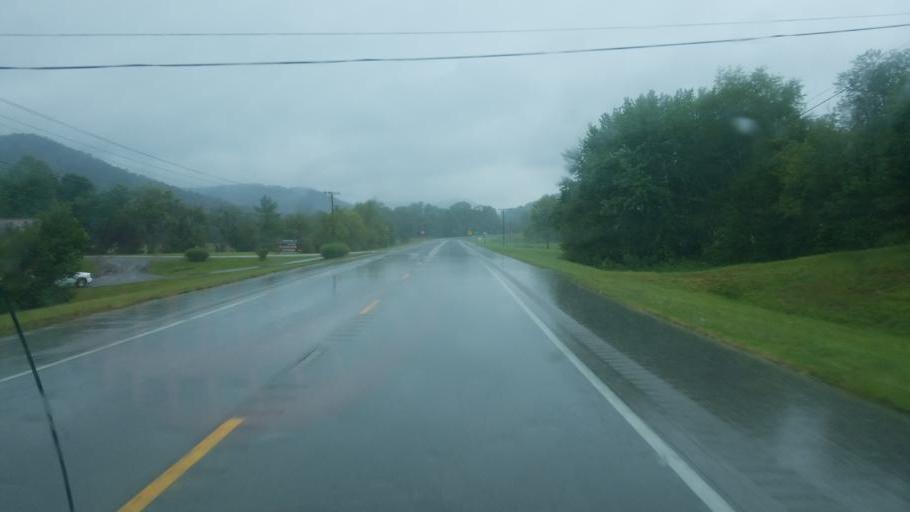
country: US
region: Kentucky
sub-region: Lewis County
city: Vanceburg
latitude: 38.5767
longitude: -83.4293
